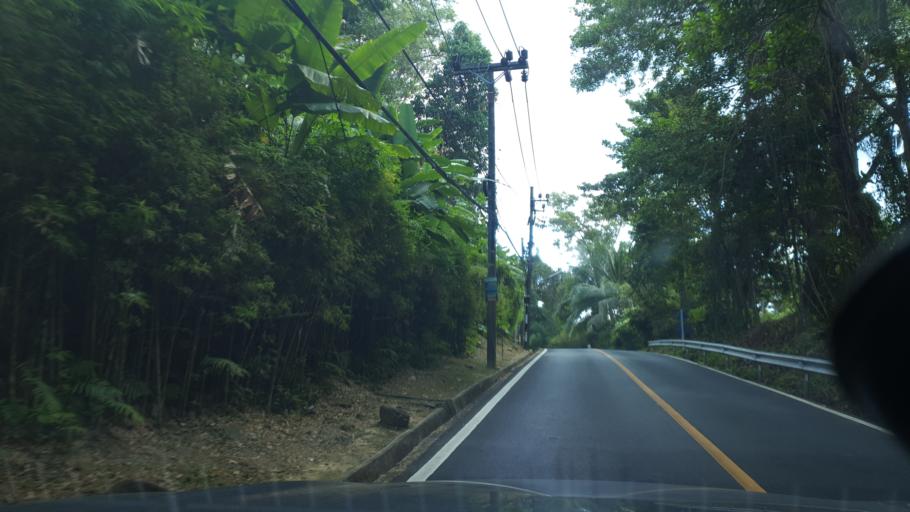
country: TH
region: Phuket
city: Thalang
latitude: 8.0518
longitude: 98.2775
